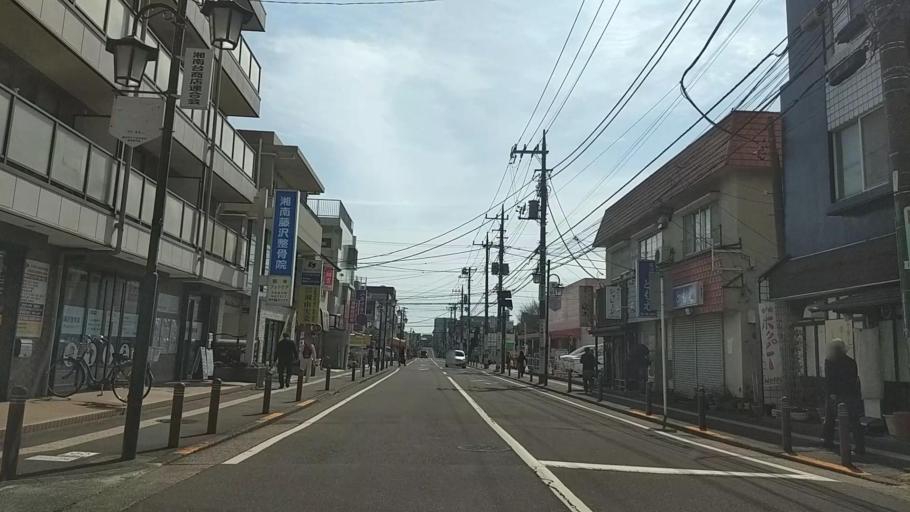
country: JP
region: Kanagawa
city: Fujisawa
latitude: 35.3951
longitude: 139.4654
